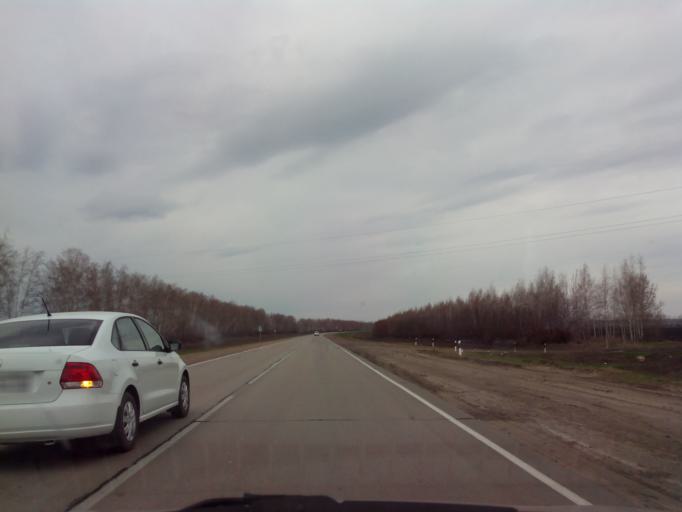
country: RU
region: Tambov
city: Znamenka
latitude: 52.4081
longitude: 41.3845
